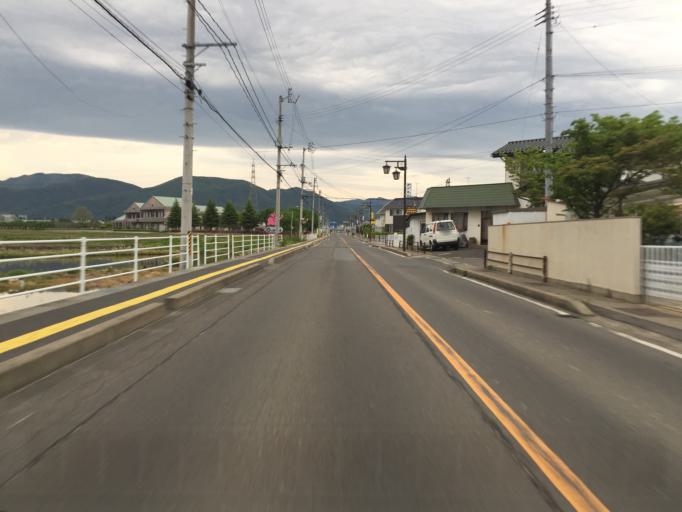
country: JP
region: Fukushima
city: Fukushima-shi
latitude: 37.7923
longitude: 140.4334
